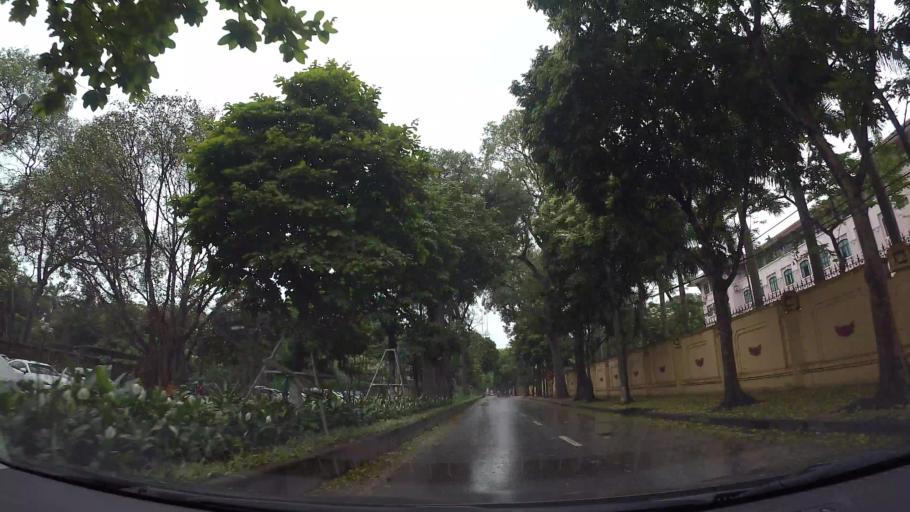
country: VN
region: Ha Noi
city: Hoan Kiem
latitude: 21.0377
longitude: 105.8415
